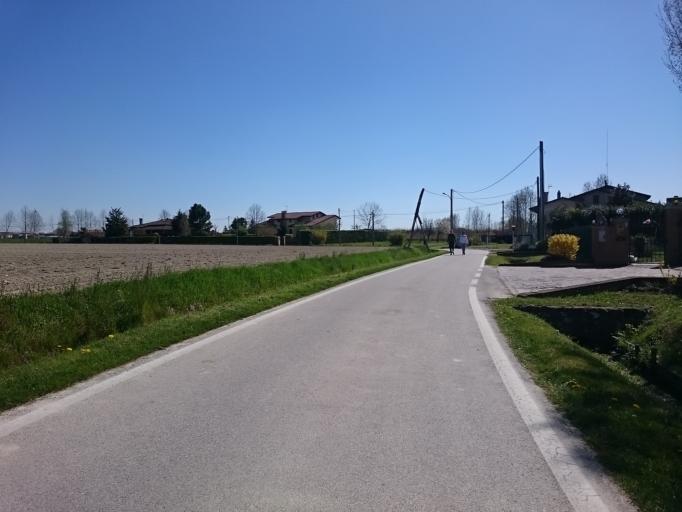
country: IT
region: Veneto
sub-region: Provincia di Padova
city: Legnaro
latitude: 45.3361
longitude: 11.9537
